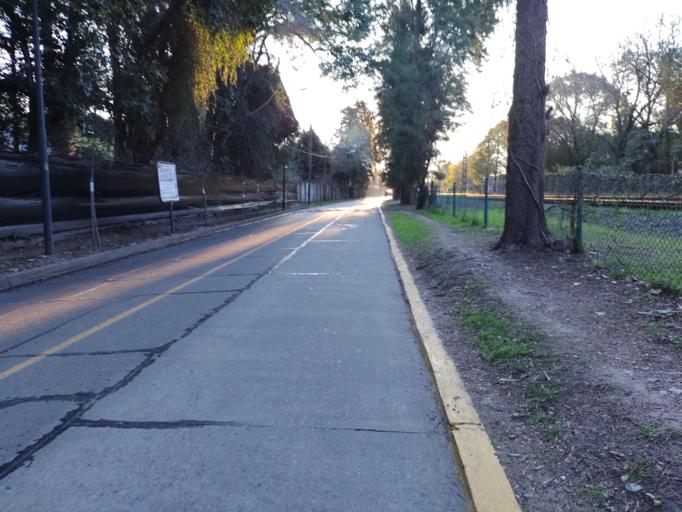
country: AR
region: Buenos Aires
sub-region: Partido de San Isidro
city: San Isidro
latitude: -34.4475
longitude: -58.5292
